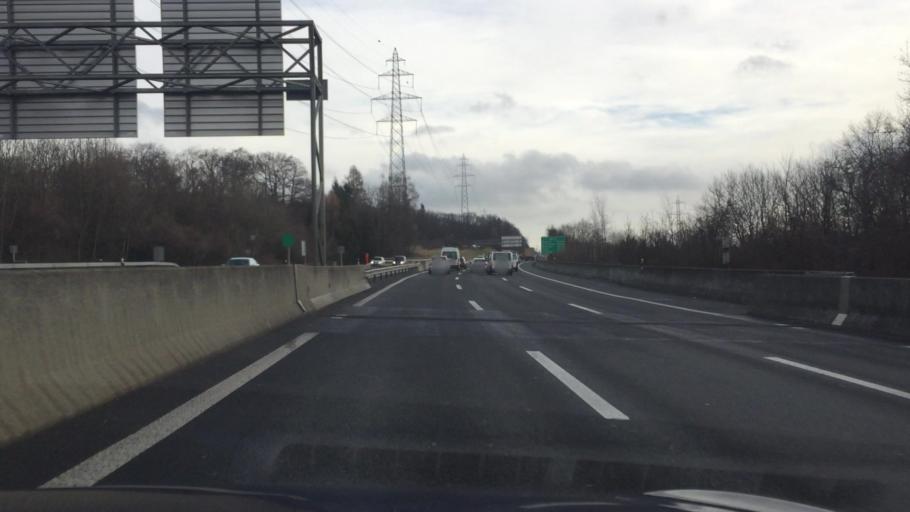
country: CH
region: Vaud
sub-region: Ouest Lausannois District
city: Crissier
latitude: 46.5644
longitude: 6.5710
